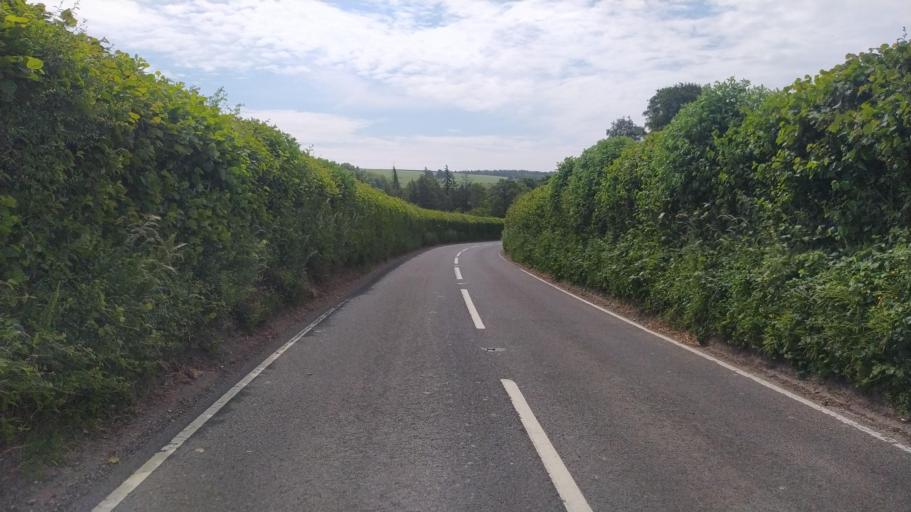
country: GB
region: England
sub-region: Dorset
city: Dorchester
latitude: 50.7898
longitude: -2.4742
